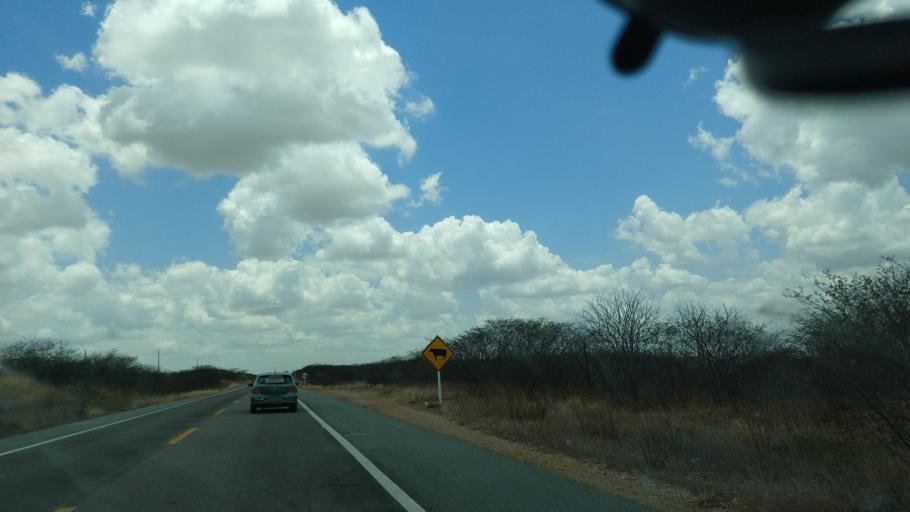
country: BR
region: Rio Grande do Norte
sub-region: Cerro Cora
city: Cerro Cora
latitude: -6.2079
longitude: -36.2868
